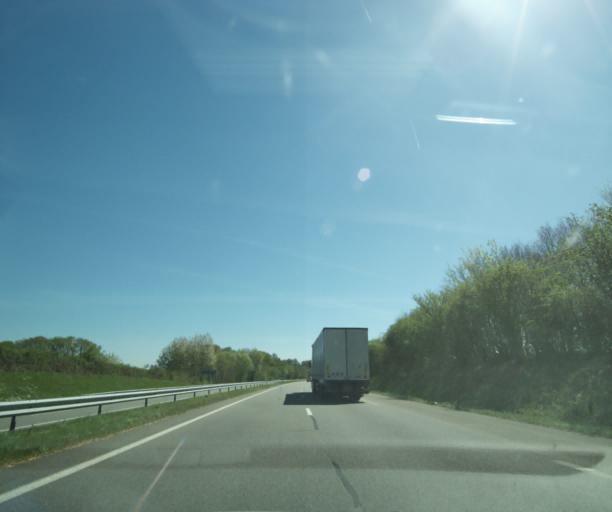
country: FR
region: Limousin
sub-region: Departement de la Correze
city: Uzerche
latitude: 45.4932
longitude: 1.5265
